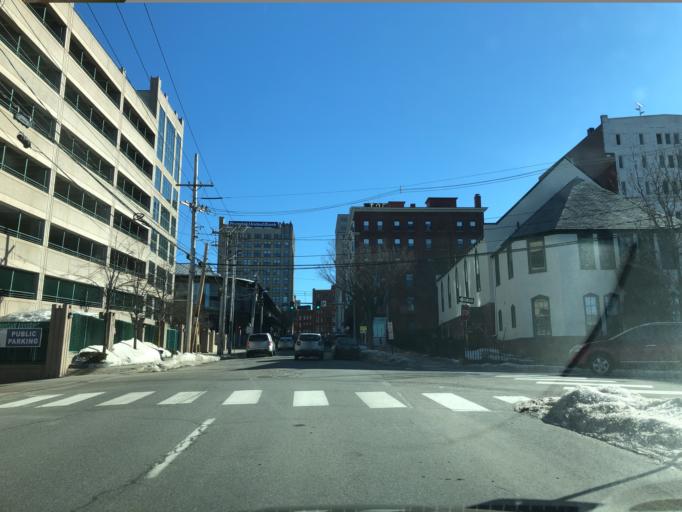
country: US
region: Maine
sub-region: Cumberland County
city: Portland
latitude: 43.6589
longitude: -70.2616
